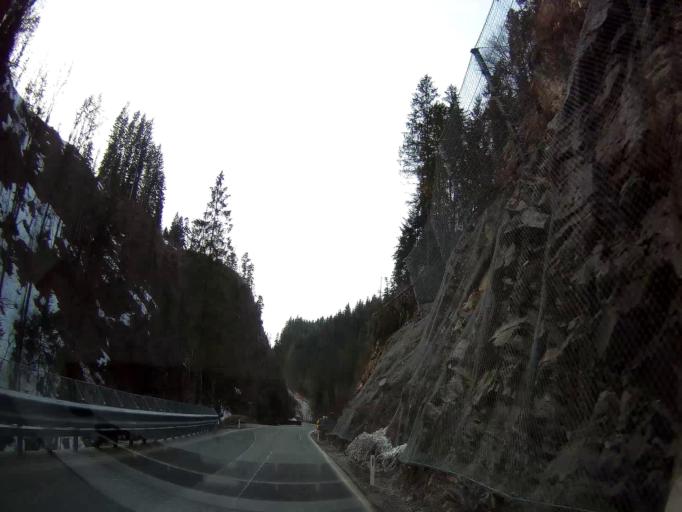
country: AT
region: Salzburg
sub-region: Politischer Bezirk Hallein
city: Abtenau
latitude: 47.5442
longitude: 13.4205
